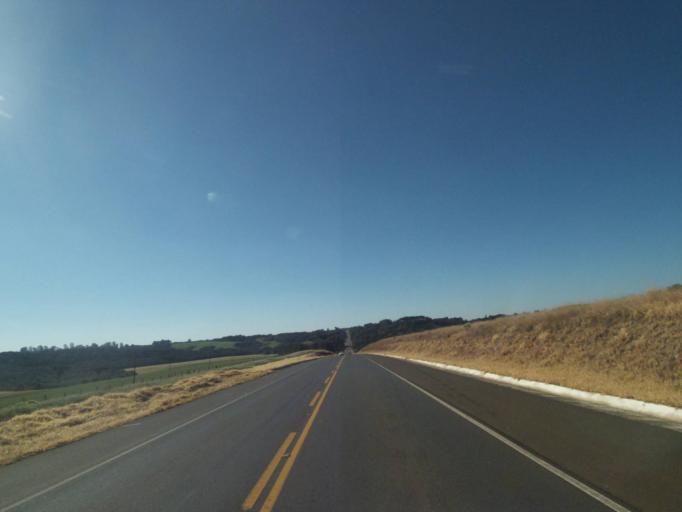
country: BR
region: Parana
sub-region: Tibagi
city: Tibagi
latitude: -24.6187
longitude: -50.4488
